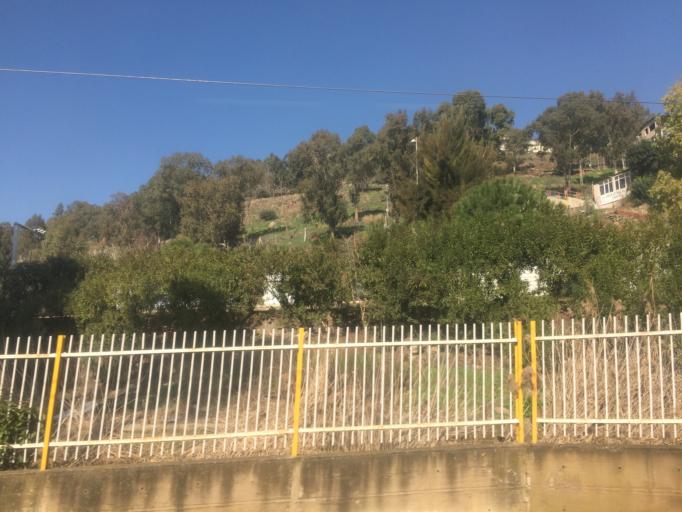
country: TR
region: Izmir
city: Karsiyaka
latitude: 38.4681
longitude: 27.1538
